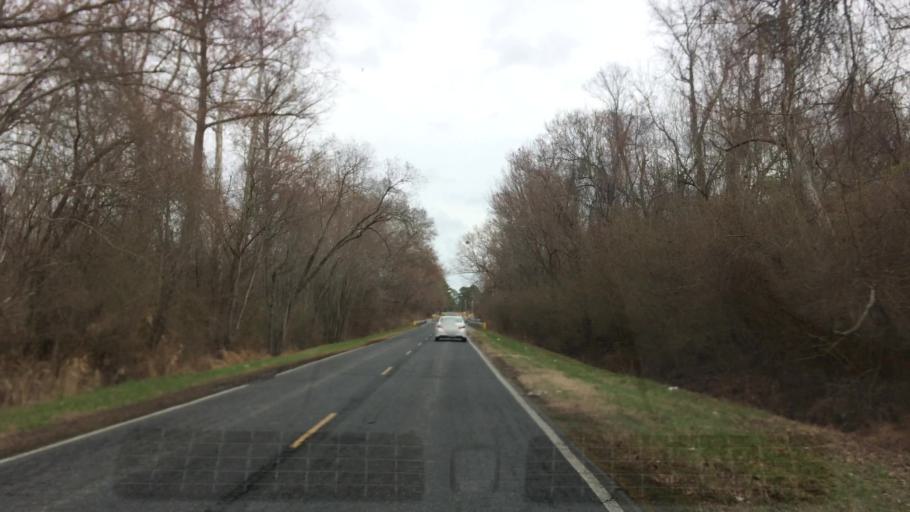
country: US
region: North Carolina
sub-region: Pitt County
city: Ayden
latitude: 35.4885
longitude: -77.3685
